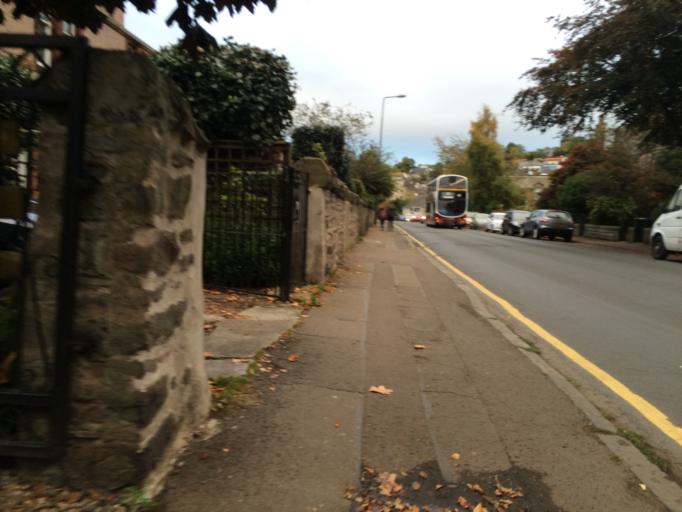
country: GB
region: Scotland
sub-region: Edinburgh
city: Edinburgh
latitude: 55.9287
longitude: -3.1883
